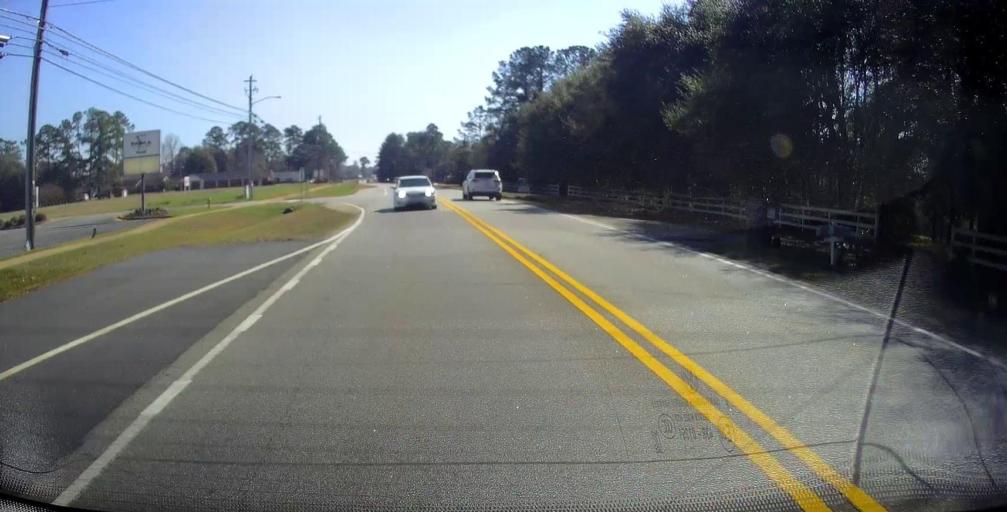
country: US
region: Georgia
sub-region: Houston County
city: Perry
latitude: 32.4771
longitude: -83.7300
